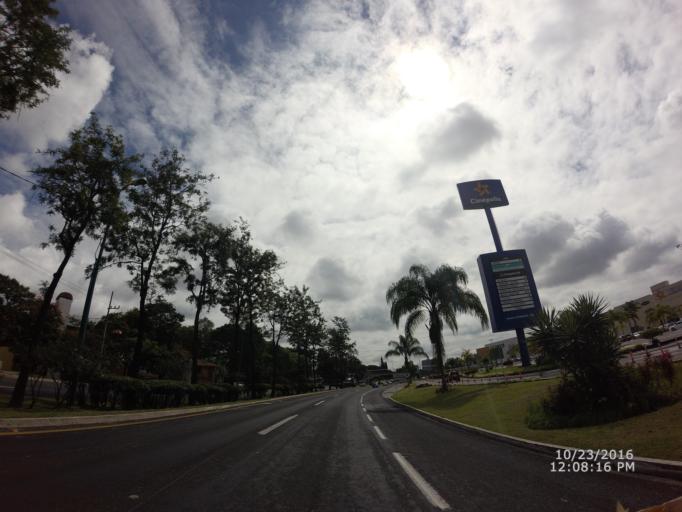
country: MX
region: Veracruz
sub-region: Xalapa
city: Colonia Santa Barbara
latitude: 19.5144
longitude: -96.8769
